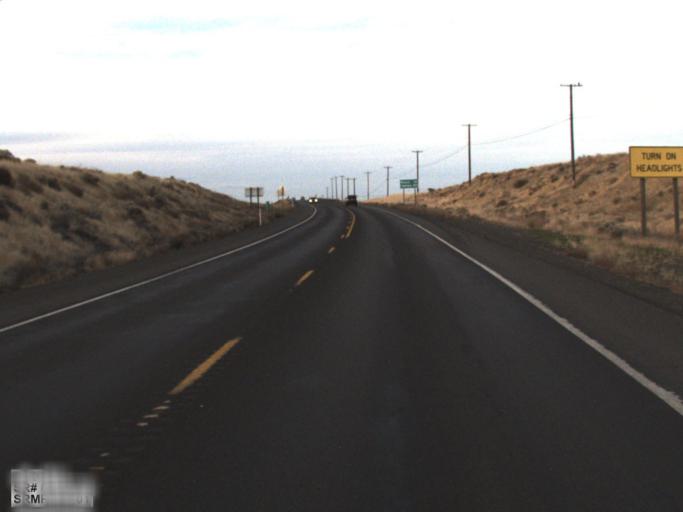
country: US
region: Washington
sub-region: Benton County
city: Finley
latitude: 46.0648
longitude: -118.9081
